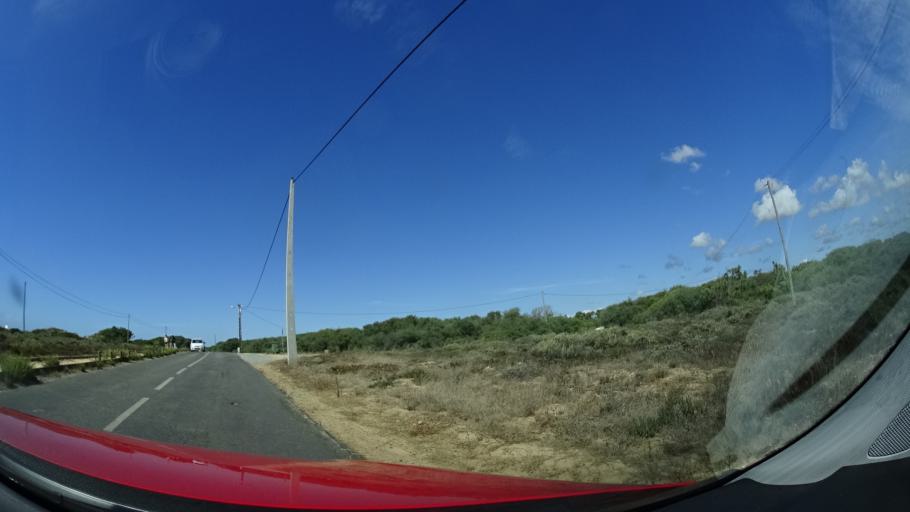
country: PT
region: Beja
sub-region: Odemira
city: Sao Teotonio
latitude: 37.5324
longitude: -8.7844
